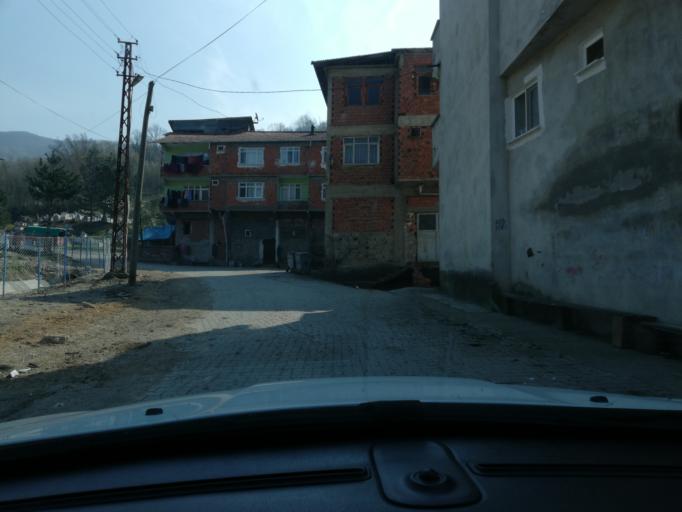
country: TR
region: Karabuk
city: Yenice
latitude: 41.2628
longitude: 32.3631
